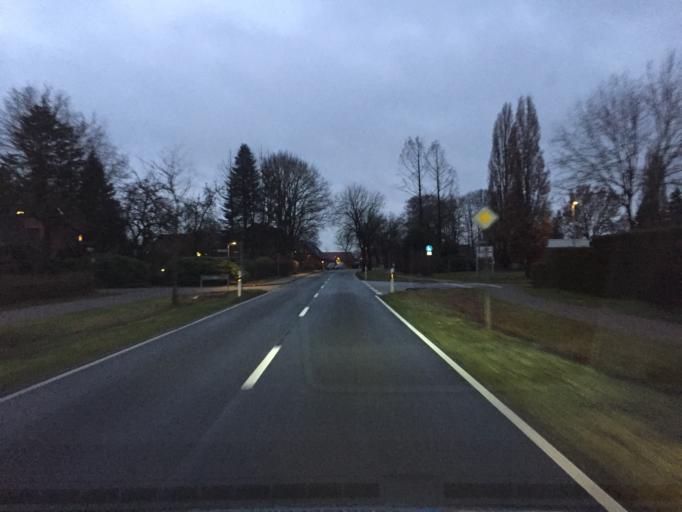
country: DE
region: Lower Saxony
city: Schwaforden
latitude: 52.7407
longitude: 8.8187
